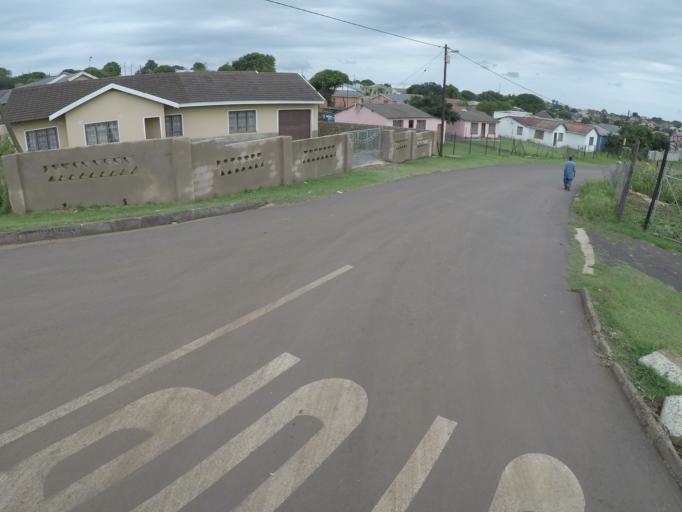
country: ZA
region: KwaZulu-Natal
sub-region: uThungulu District Municipality
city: Empangeni
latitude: -28.7728
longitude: 31.8533
